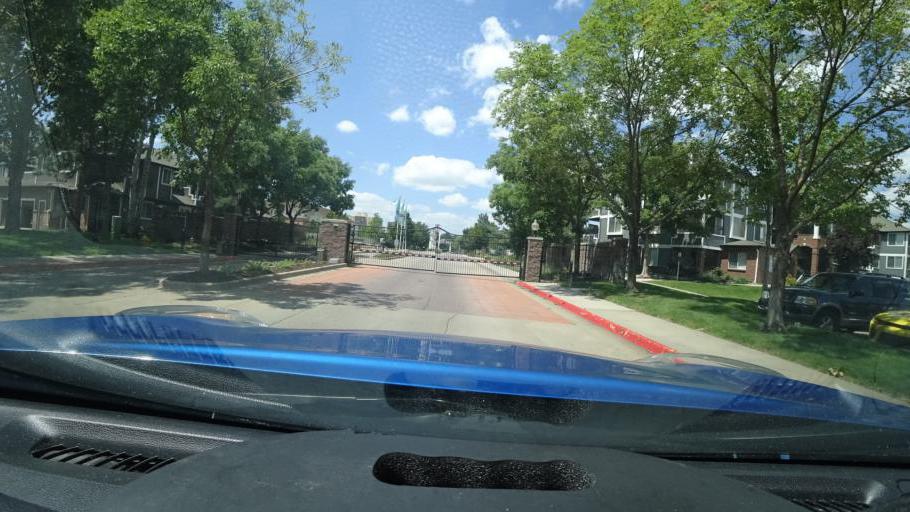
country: US
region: Colorado
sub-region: Arapahoe County
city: Glendale
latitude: 39.6983
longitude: -104.8909
